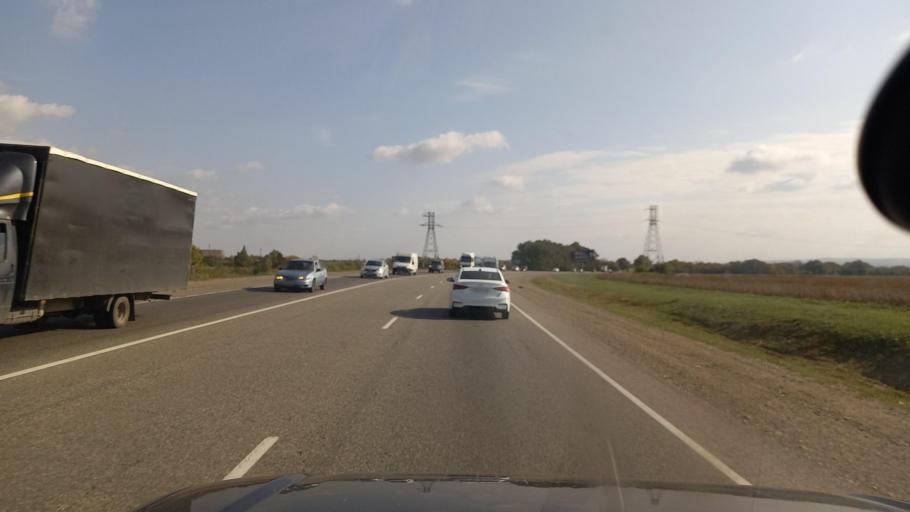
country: RU
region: Krasnodarskiy
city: Kholmskiy
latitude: 44.8549
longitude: 38.3485
